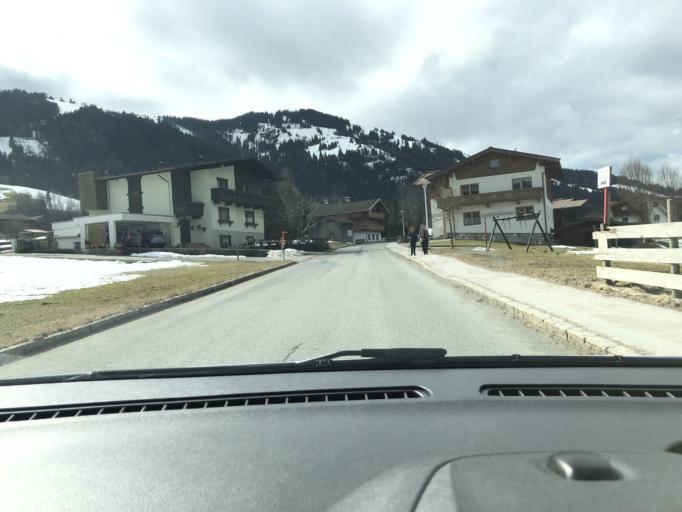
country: AT
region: Tyrol
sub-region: Politischer Bezirk Kitzbuhel
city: Itter
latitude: 47.4491
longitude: 12.1052
